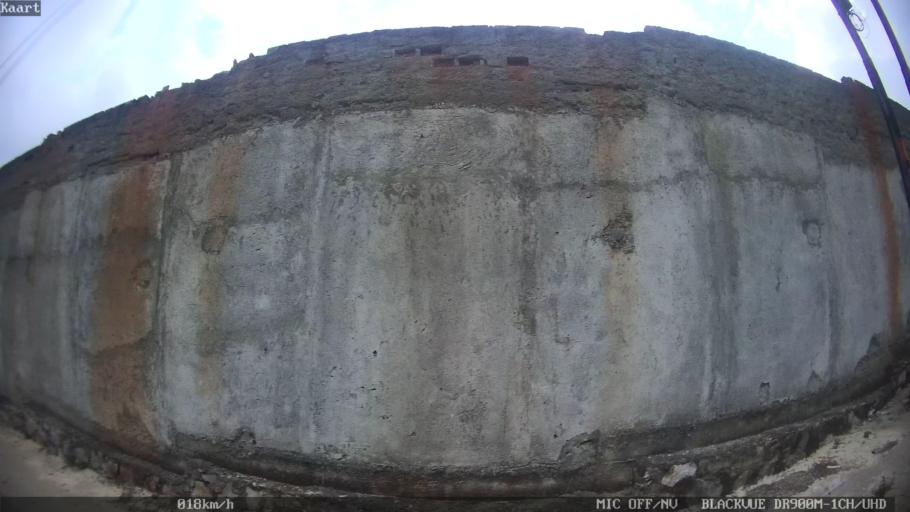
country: ID
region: Lampung
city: Bandarlampung
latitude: -5.4107
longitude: 105.2881
